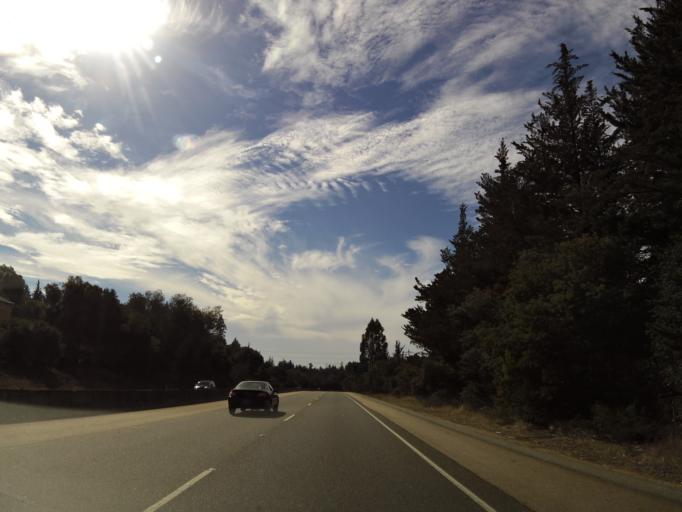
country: US
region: California
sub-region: Santa Cruz County
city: Scotts Valley
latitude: 37.0427
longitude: -122.0159
